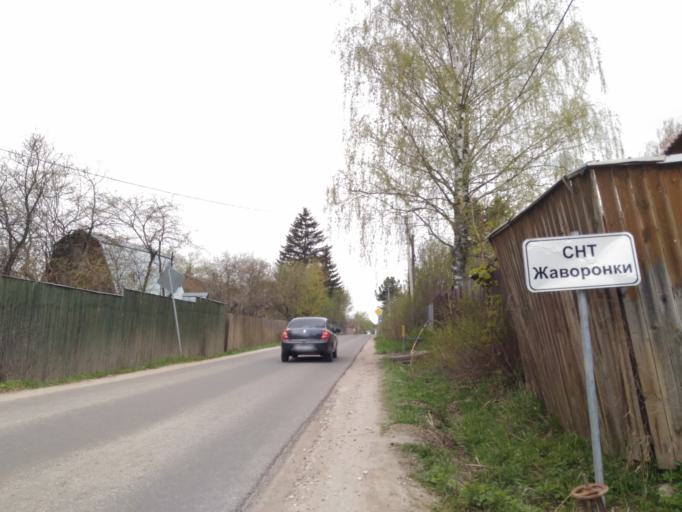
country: RU
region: Moskovskaya
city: Dedovsk
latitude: 55.8509
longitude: 37.1451
